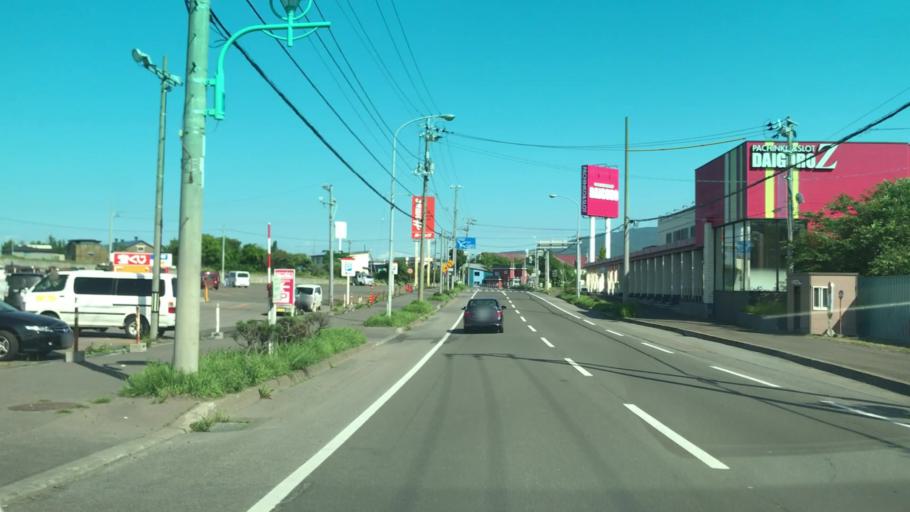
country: JP
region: Hokkaido
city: Iwanai
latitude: 42.9818
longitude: 140.5381
